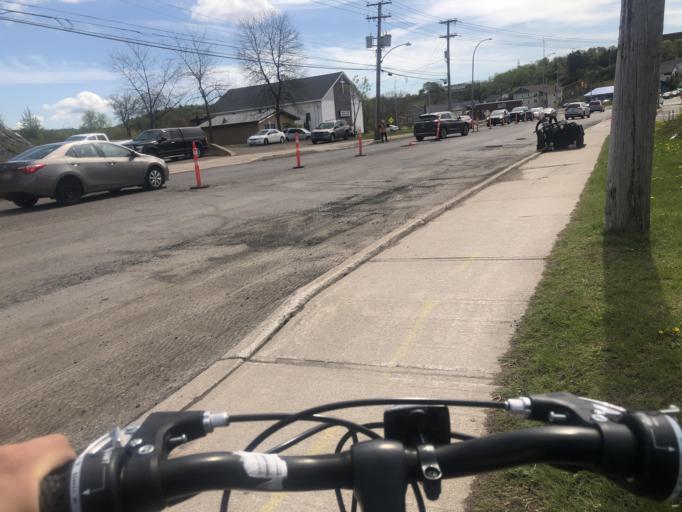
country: CA
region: New Brunswick
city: Saint John
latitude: 45.2875
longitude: -66.0802
